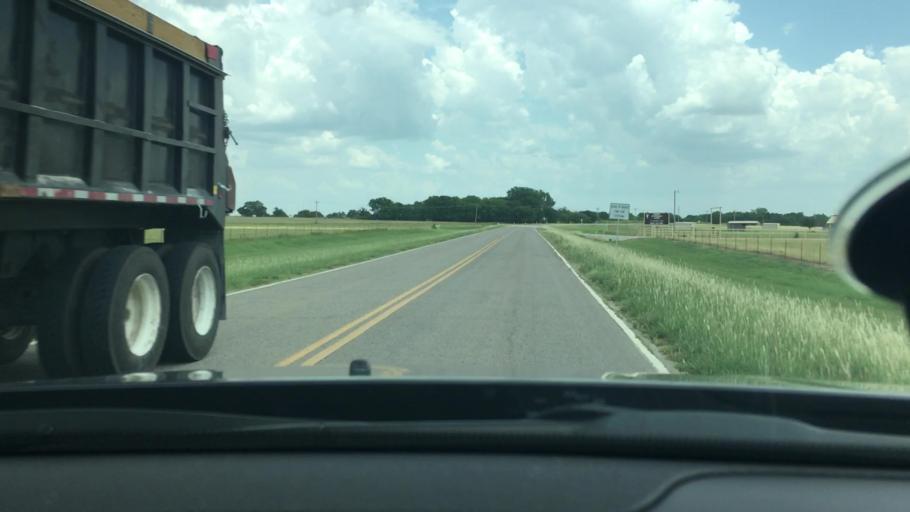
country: US
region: Oklahoma
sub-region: Love County
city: Marietta
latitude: 33.9382
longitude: -97.1040
